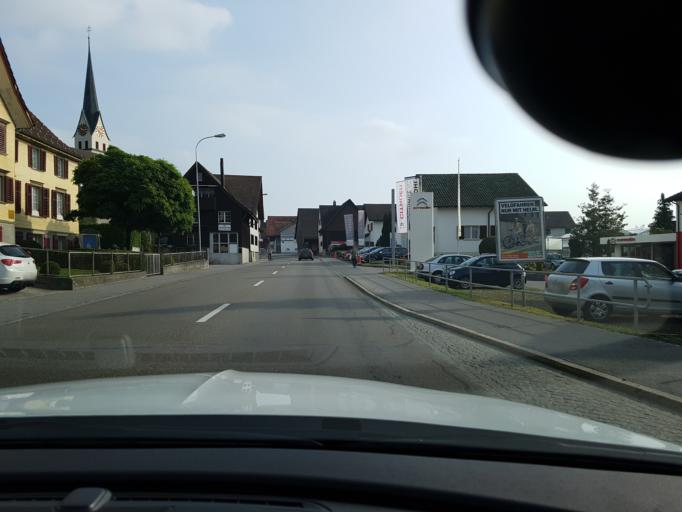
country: CH
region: Saint Gallen
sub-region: Wahlkreis Rheintal
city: Rebstein
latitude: 47.3906
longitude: 9.5662
